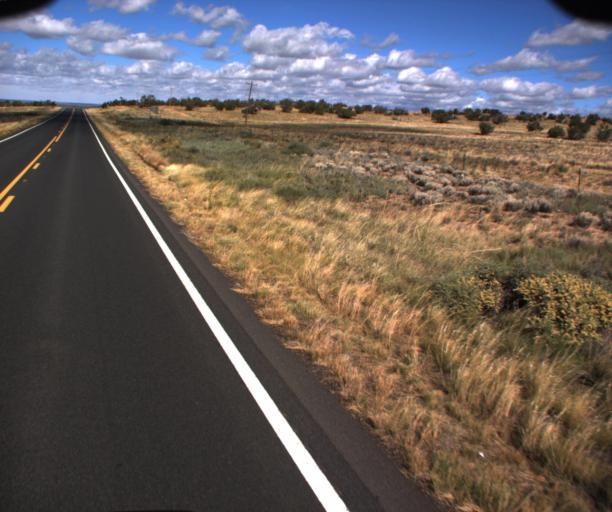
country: US
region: Arizona
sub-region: Apache County
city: Houck
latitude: 35.0722
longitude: -109.2902
